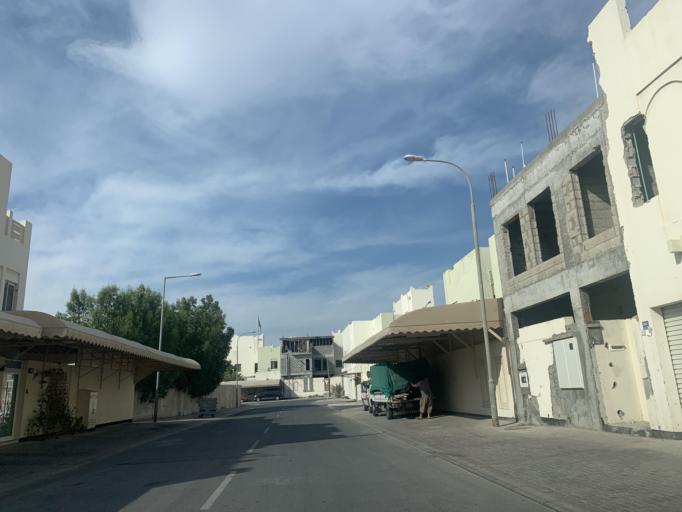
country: BH
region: Central Governorate
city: Madinat Hamad
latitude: 26.1225
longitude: 50.4753
